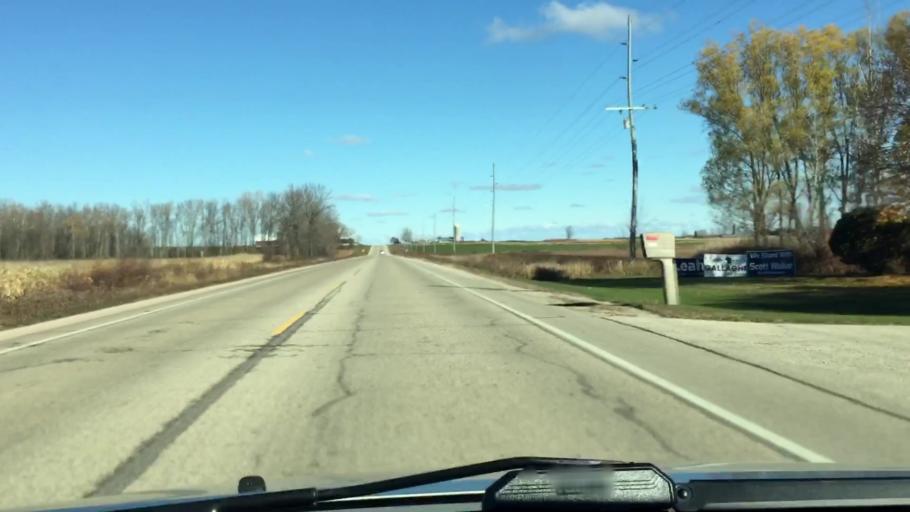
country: US
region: Wisconsin
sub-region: Oconto County
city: Gillett
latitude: 44.8572
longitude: -88.2480
